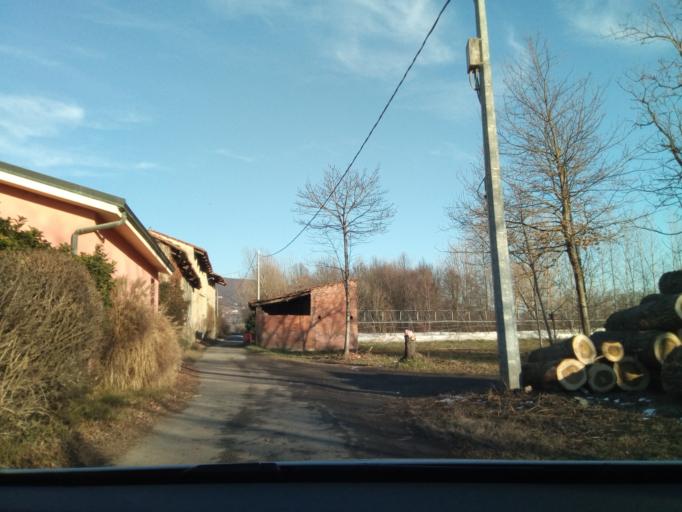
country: IT
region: Piedmont
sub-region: Provincia di Torino
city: Bollengo
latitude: 45.4616
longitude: 7.9324
